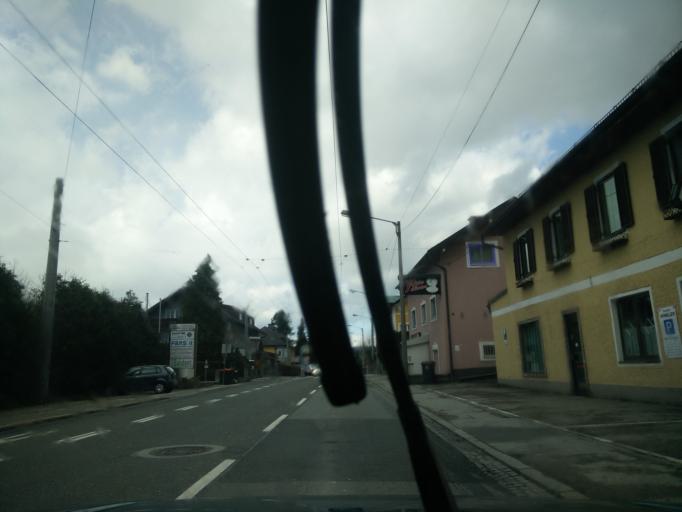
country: AT
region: Salzburg
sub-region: Politischer Bezirk Salzburg-Umgebung
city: Hallwang
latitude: 47.8231
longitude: 13.0781
